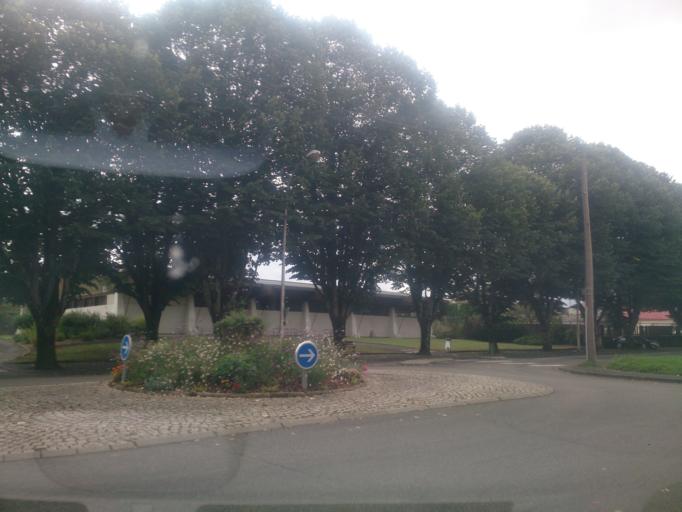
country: FR
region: Limousin
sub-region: Departement de la Correze
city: Brive-la-Gaillarde
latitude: 45.1595
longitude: 1.5428
